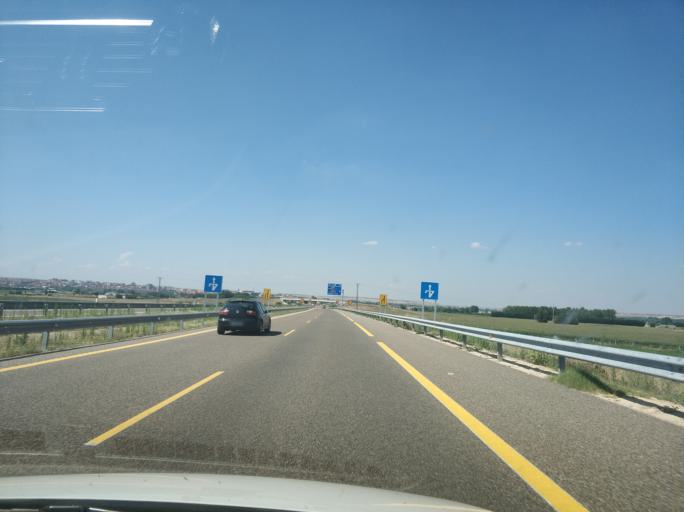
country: ES
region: Castille and Leon
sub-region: Provincia de Zamora
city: Morales del Vino
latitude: 41.4756
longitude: -5.7195
